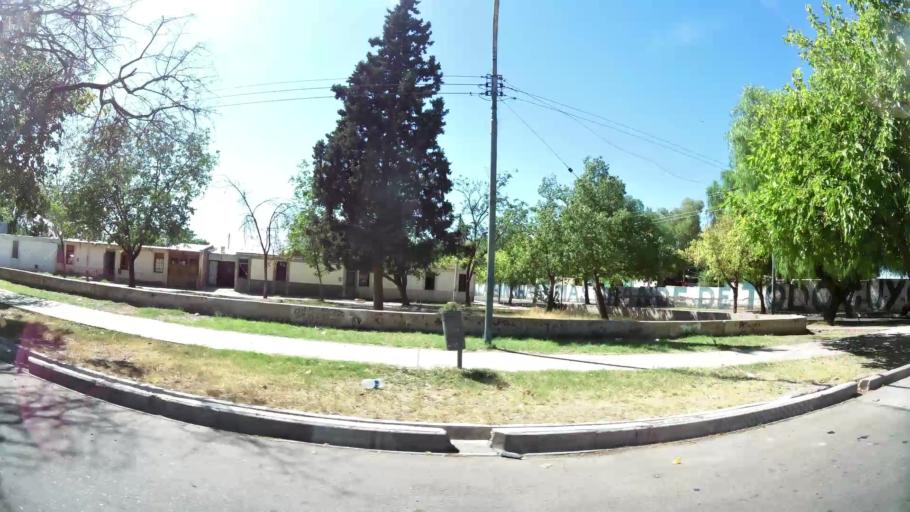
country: AR
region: Mendoza
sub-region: Departamento de Godoy Cruz
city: Godoy Cruz
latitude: -32.9073
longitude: -68.8705
